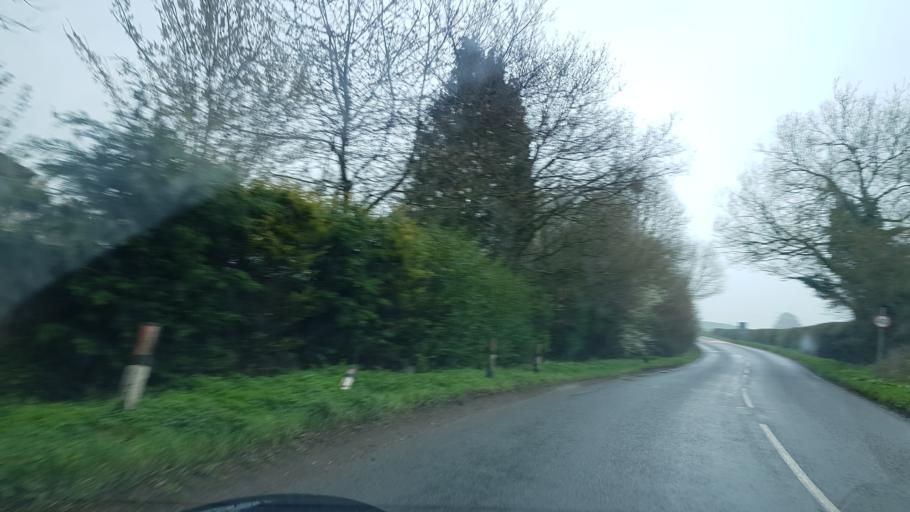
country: GB
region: England
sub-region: Herefordshire
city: Donnington
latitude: 51.9767
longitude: -2.4315
